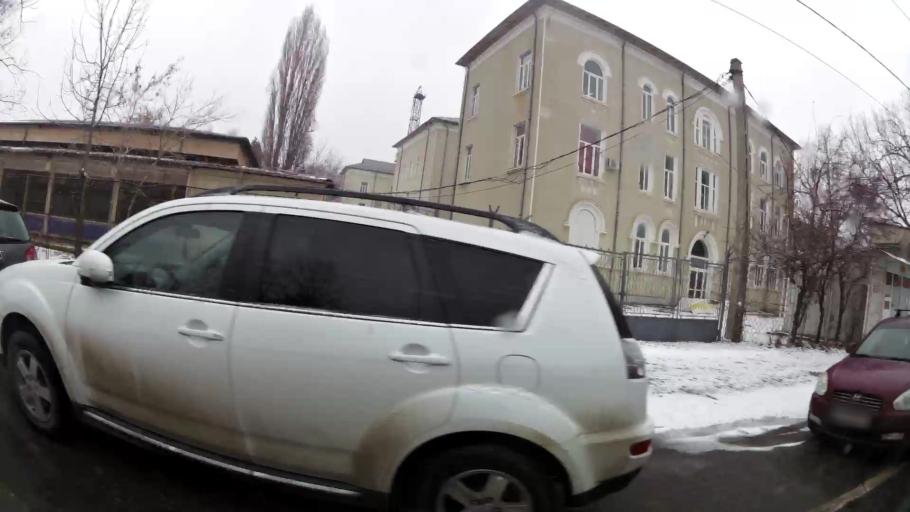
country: RO
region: Dambovita
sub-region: Municipiul Targoviste
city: Targoviste
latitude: 44.9171
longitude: 25.4535
